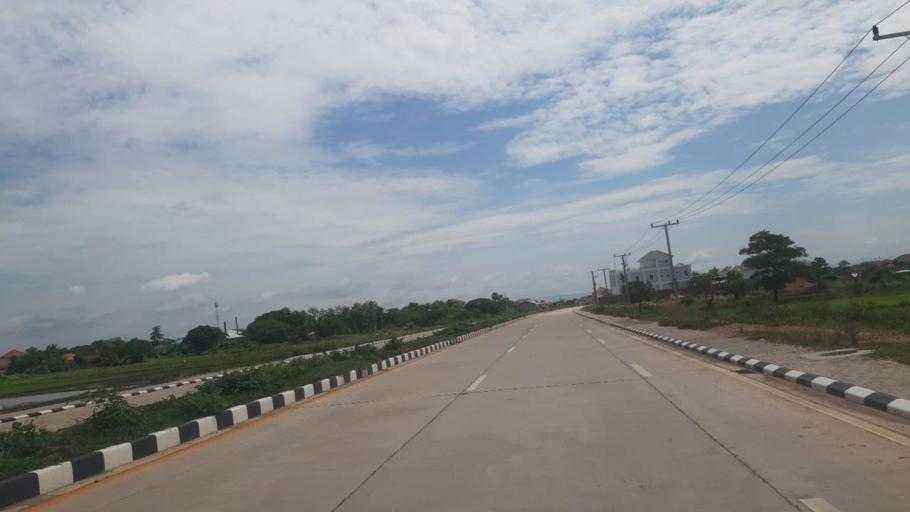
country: LA
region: Vientiane
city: Vientiane
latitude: 18.0348
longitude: 102.6115
